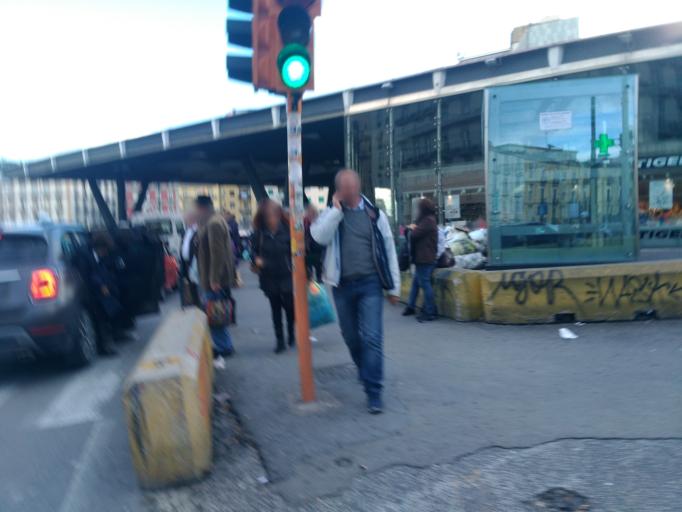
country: IT
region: Campania
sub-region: Provincia di Napoli
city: Napoli
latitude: 40.8519
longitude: 14.2719
